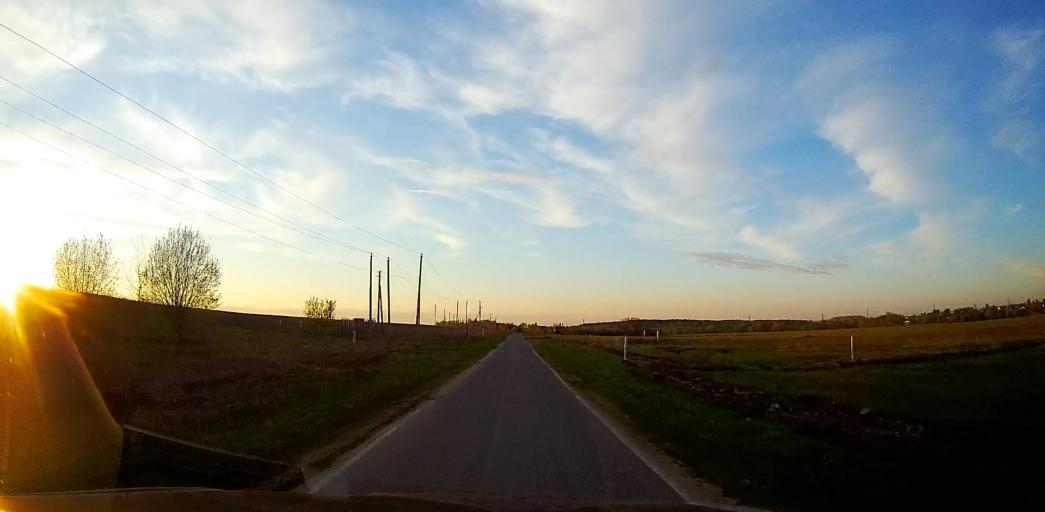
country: RU
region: Moskovskaya
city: Peski
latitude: 55.2218
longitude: 38.7362
